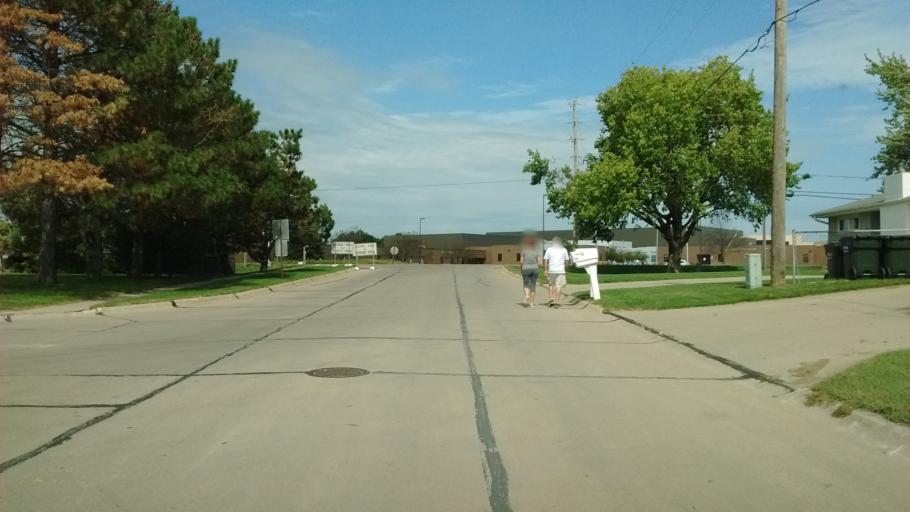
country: US
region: South Dakota
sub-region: Union County
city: North Sioux City
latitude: 42.5472
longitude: -96.5241
